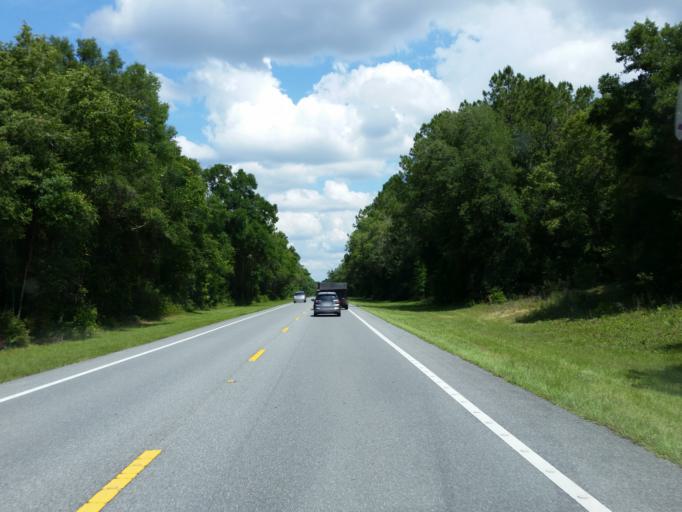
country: US
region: Florida
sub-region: Citrus County
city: Hernando
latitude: 28.9214
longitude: -82.3887
